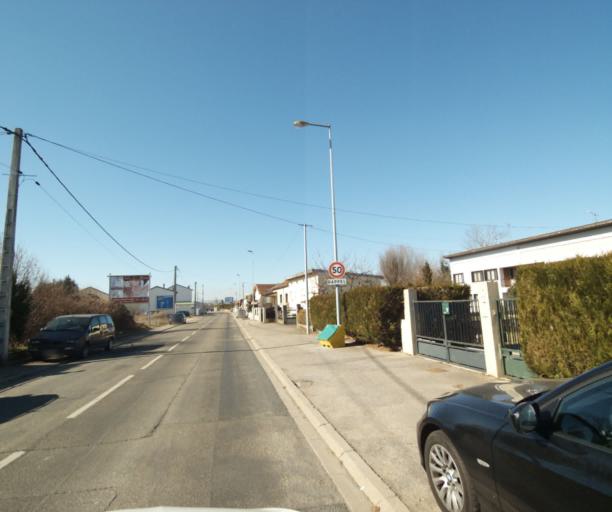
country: FR
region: Lorraine
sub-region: Departement de Meurthe-et-Moselle
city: Saulxures-les-Nancy
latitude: 48.6836
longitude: 6.2316
